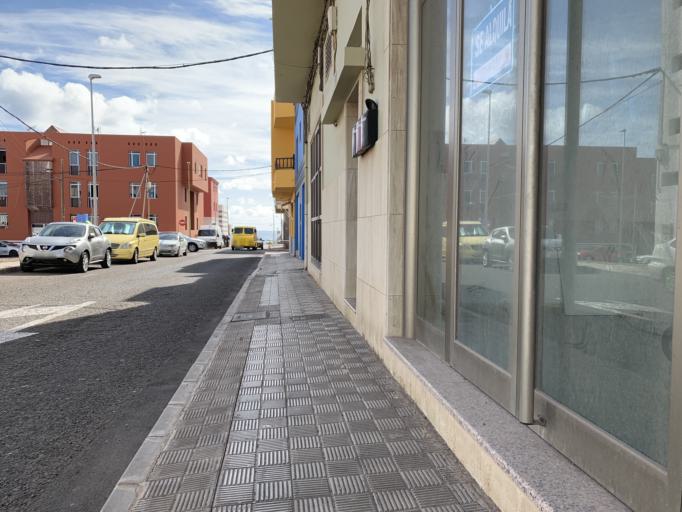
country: ES
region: Canary Islands
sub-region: Provincia de Las Palmas
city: Puerto del Rosario
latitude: 28.5029
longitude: -13.8488
